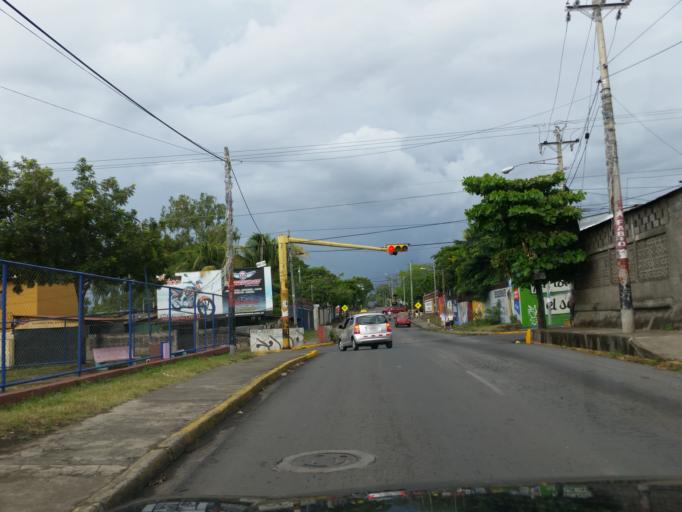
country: NI
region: Managua
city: Managua
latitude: 12.1074
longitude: -86.2979
